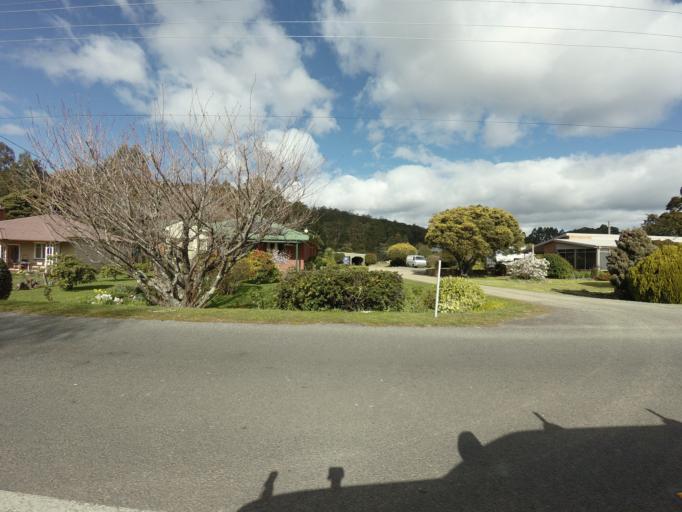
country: AU
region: Tasmania
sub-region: Huon Valley
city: Geeveston
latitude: -43.1707
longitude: 146.9250
